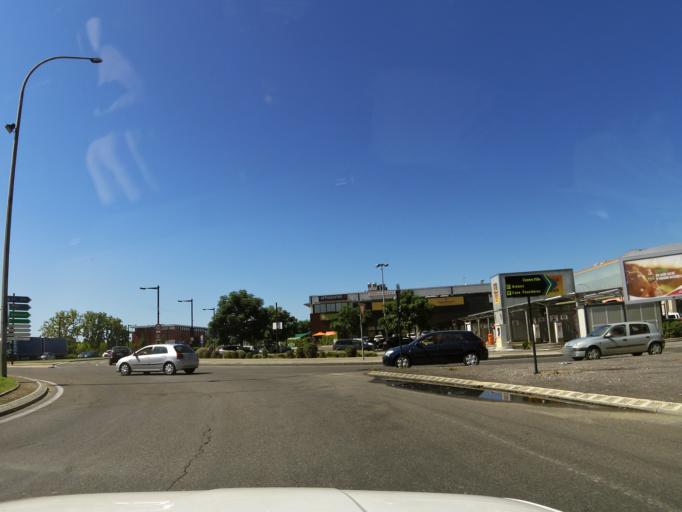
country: FR
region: Languedoc-Roussillon
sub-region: Departement du Gard
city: Nimes
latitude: 43.8245
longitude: 4.3694
